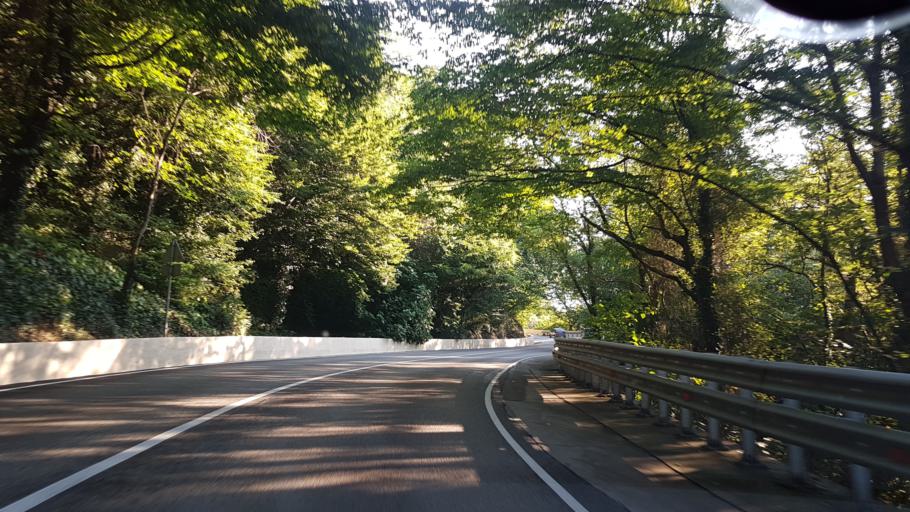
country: RU
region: Krasnodarskiy
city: Gornoye Loo
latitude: 43.6705
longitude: 39.6169
